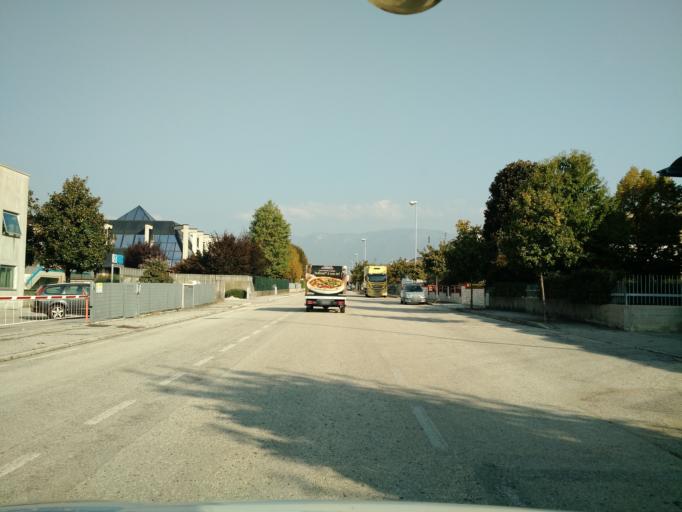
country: IT
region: Veneto
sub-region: Provincia di Vicenza
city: Thiene
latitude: 45.6795
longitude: 11.4709
